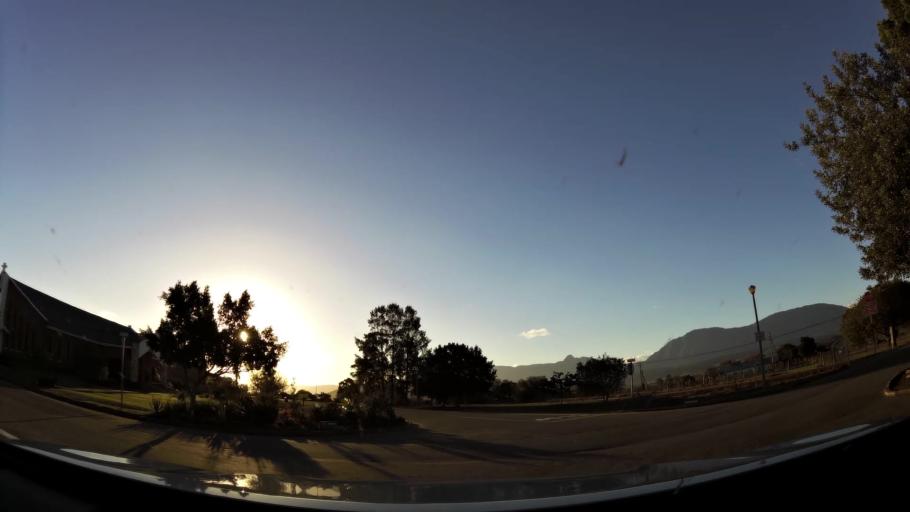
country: ZA
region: Western Cape
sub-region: Eden District Municipality
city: Riversdale
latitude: -34.0817
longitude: 21.2477
